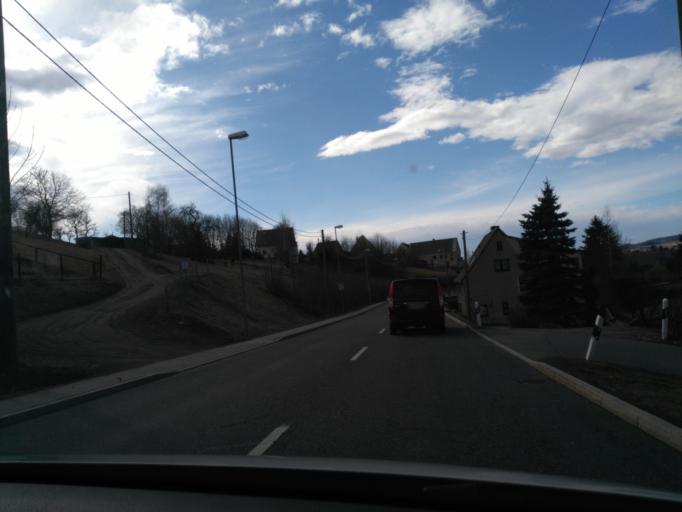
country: DE
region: Saxony
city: Wolkenstein
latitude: 50.6617
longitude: 13.0974
